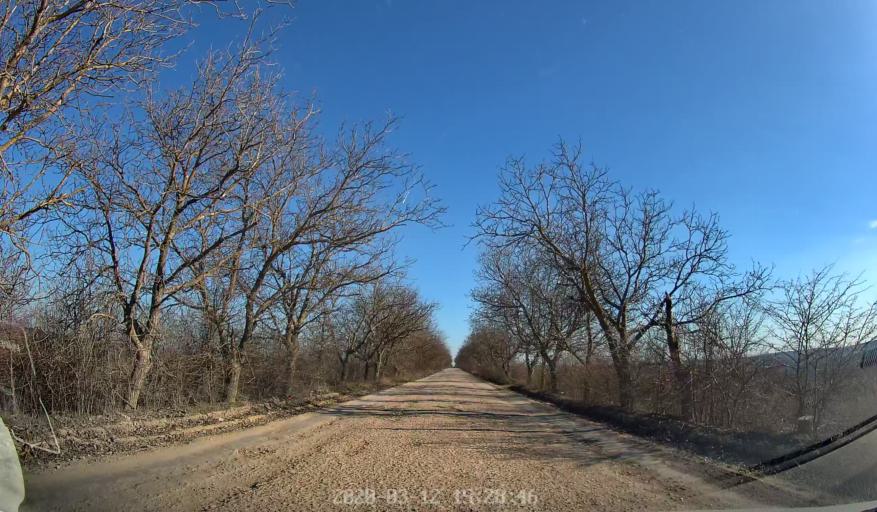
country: MD
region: Chisinau
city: Ciorescu
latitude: 47.1672
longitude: 28.9325
